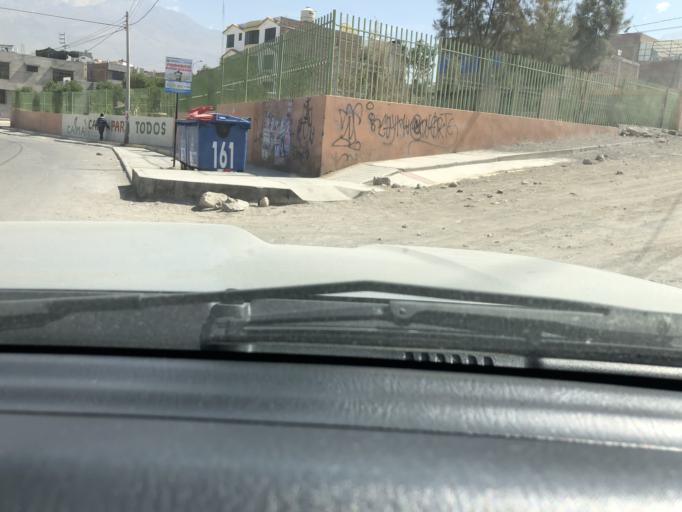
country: PE
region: Arequipa
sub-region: Provincia de Arequipa
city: Arequipa
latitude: -16.3405
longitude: -71.5518
